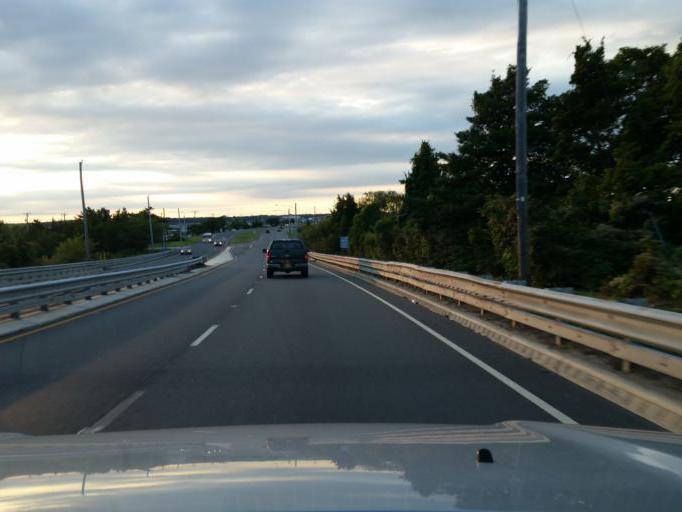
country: US
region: New Jersey
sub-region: Cape May County
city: Wildwood Crest
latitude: 38.9917
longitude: -74.8348
